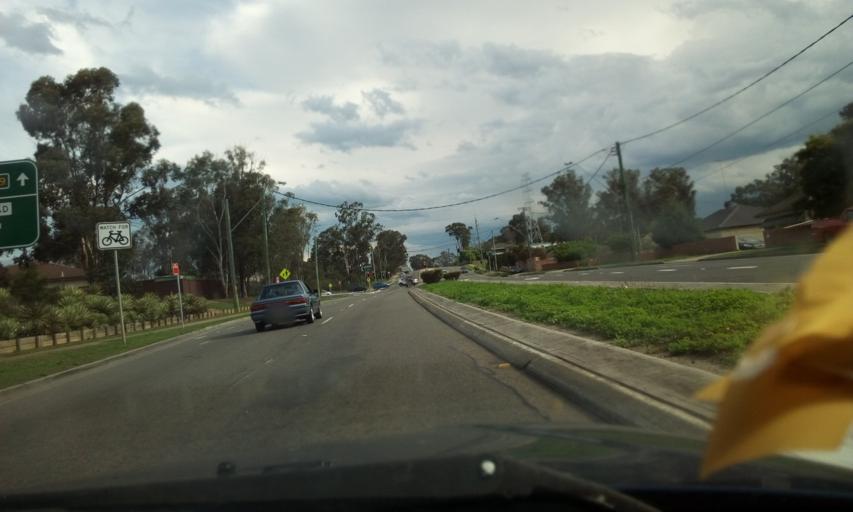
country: AU
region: New South Wales
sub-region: Penrith Municipality
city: Cambridge Park
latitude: -33.7410
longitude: 150.7164
